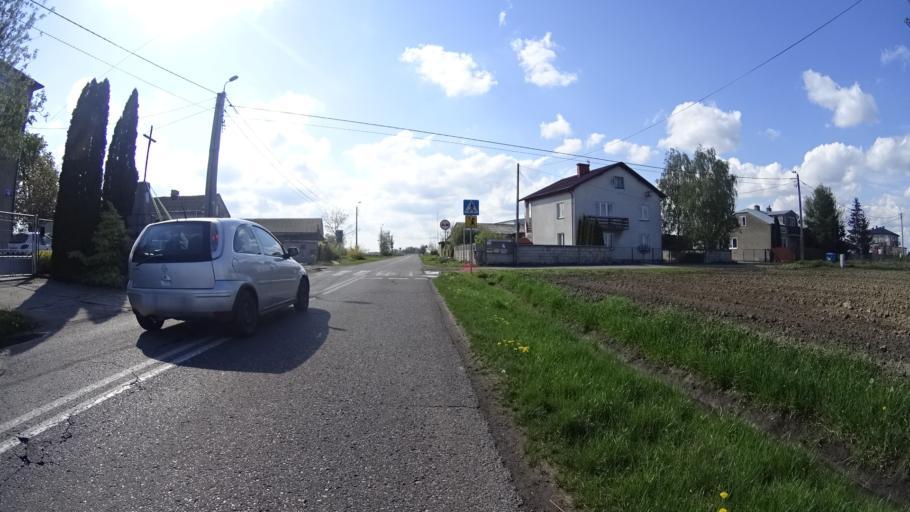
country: PL
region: Masovian Voivodeship
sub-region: Powiat warszawski zachodni
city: Jozefow
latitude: 52.2342
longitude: 20.6769
